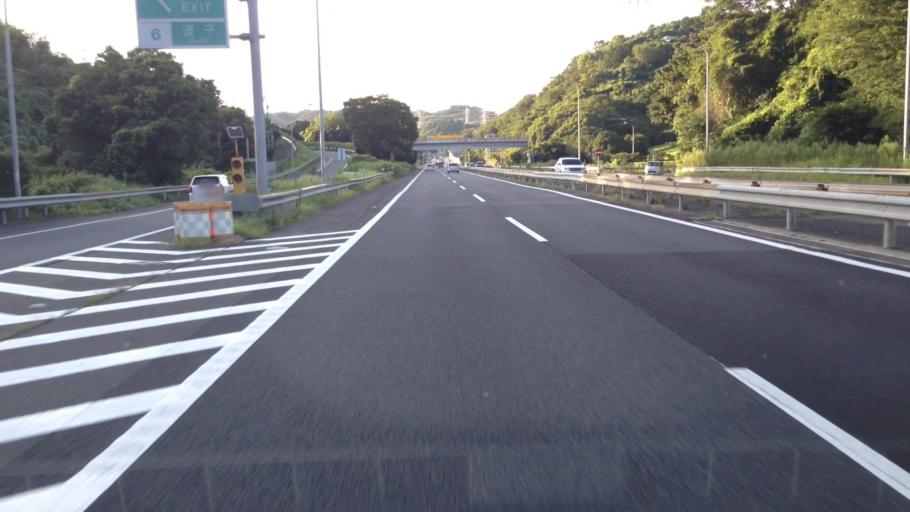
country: JP
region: Kanagawa
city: Zushi
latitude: 35.2895
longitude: 139.6201
